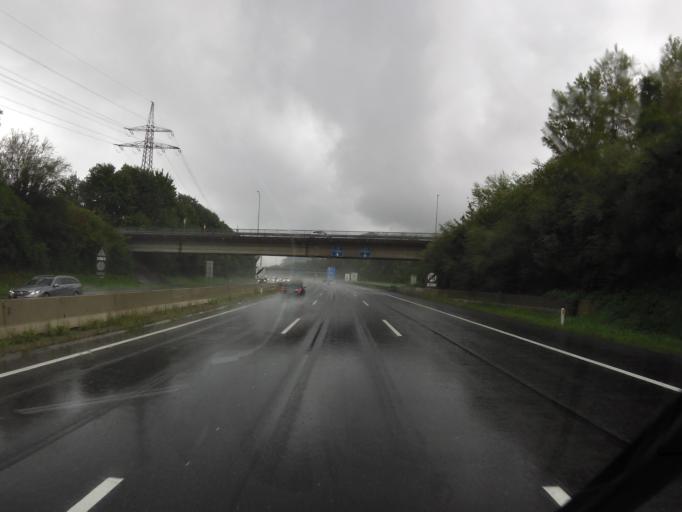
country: AT
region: Vorarlberg
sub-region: Politischer Bezirk Bregenz
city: Wolfurt
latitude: 47.4698
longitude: 9.7385
